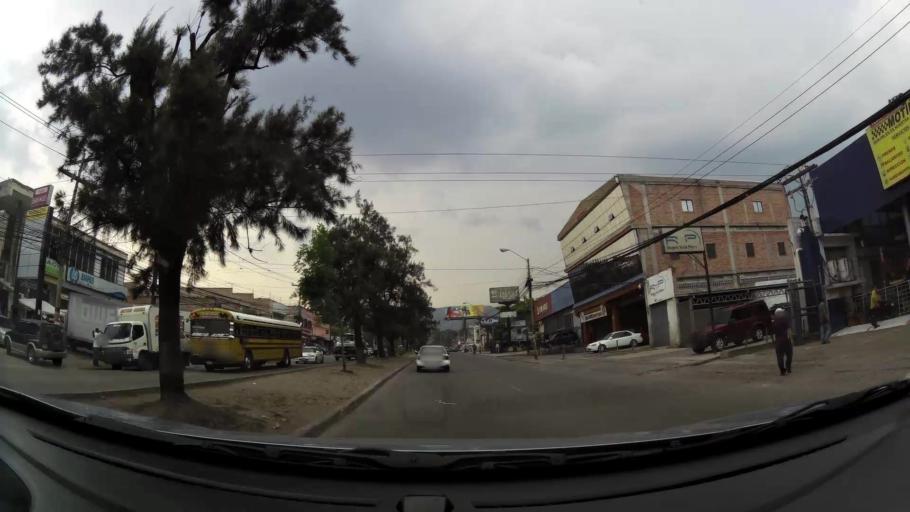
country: HN
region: Francisco Morazan
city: Tegucigalpa
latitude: 14.0994
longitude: -87.2286
